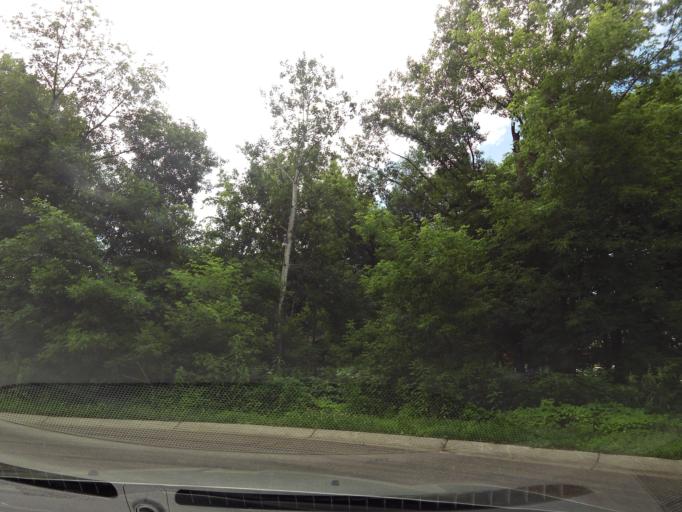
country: US
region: Minnesota
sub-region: Scott County
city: Prior Lake
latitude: 44.7526
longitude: -93.4524
